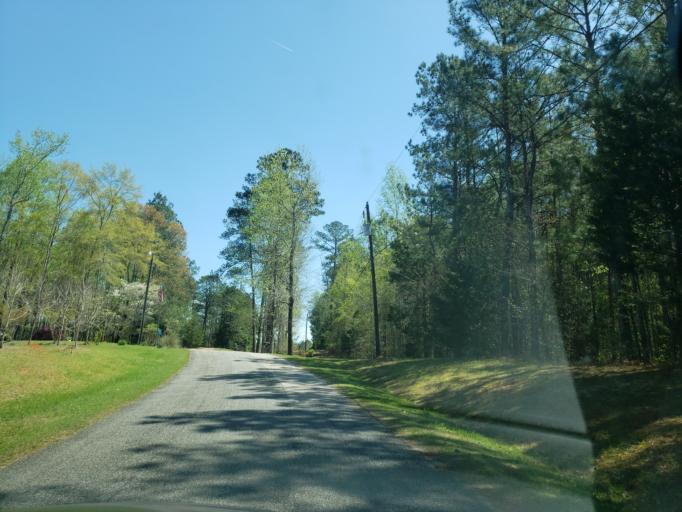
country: US
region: Alabama
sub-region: Elmore County
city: Tallassee
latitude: 32.6665
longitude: -85.8489
